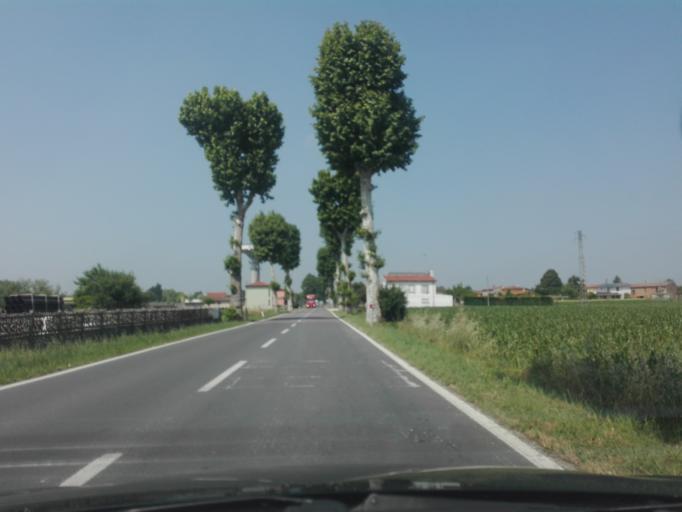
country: IT
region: Veneto
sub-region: Provincia di Rovigo
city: Villadose
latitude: 45.0653
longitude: 11.9067
